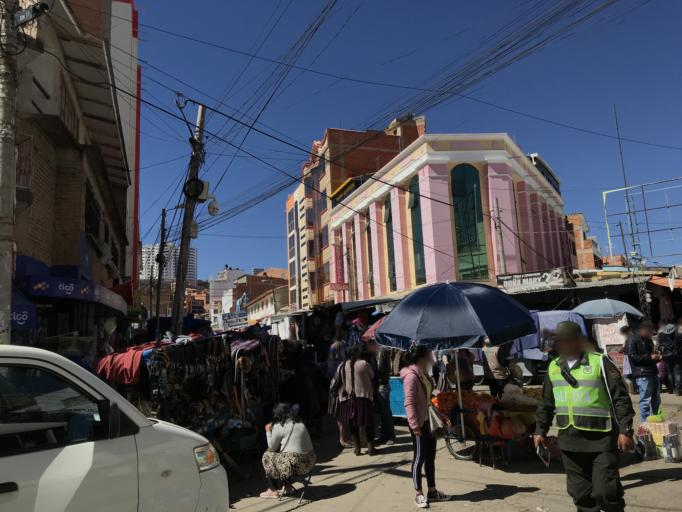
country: BO
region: Chuquisaca
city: Sucre
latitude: -19.0337
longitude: -65.2546
